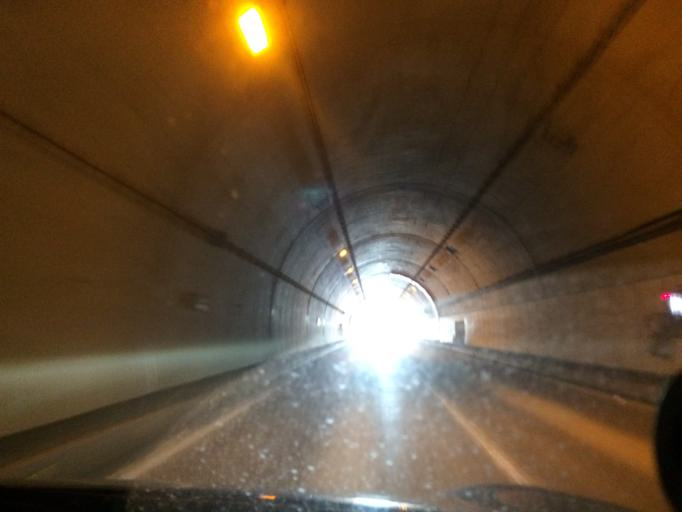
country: JP
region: Hokkaido
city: Shimo-furano
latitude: 43.0420
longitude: 142.4639
